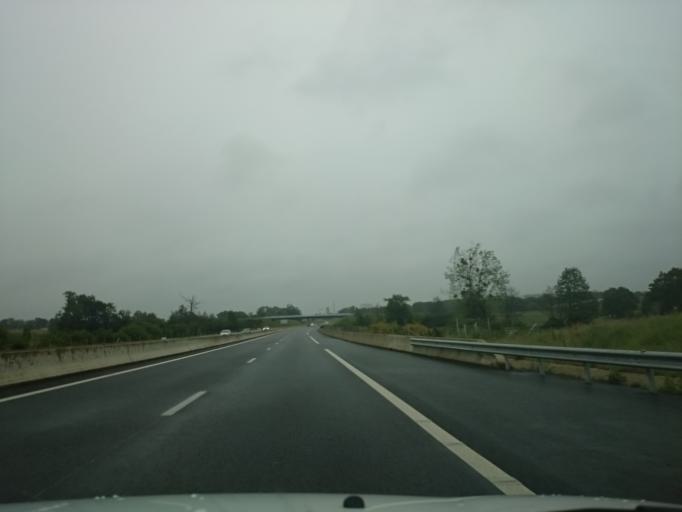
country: FR
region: Brittany
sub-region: Departement d'Ille-et-Vilaine
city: Vezin-le-Coquet
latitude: 48.1257
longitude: -1.7301
